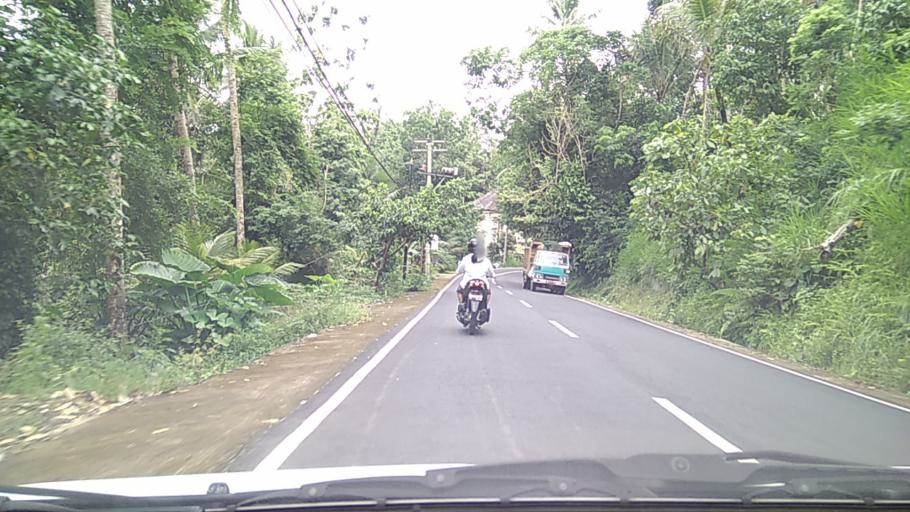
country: ID
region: Bali
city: Bangli
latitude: -8.4521
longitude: 115.3829
